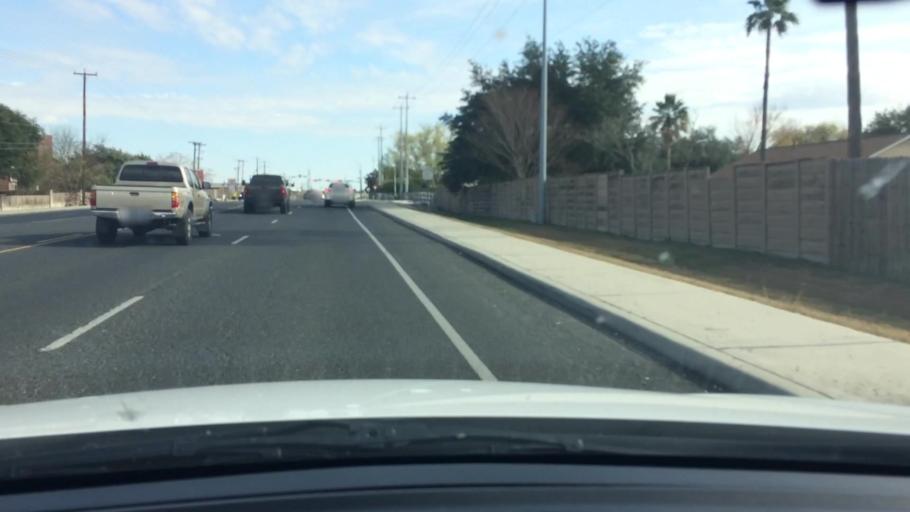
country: US
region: Texas
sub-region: Bexar County
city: Converse
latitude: 29.4883
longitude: -98.3404
